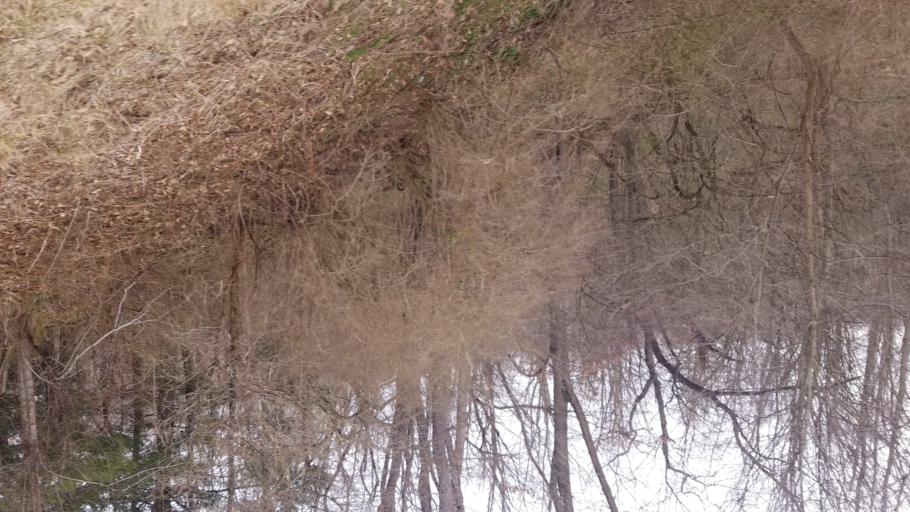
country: US
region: Ohio
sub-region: Richland County
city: Mansfield
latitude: 40.7252
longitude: -82.4891
